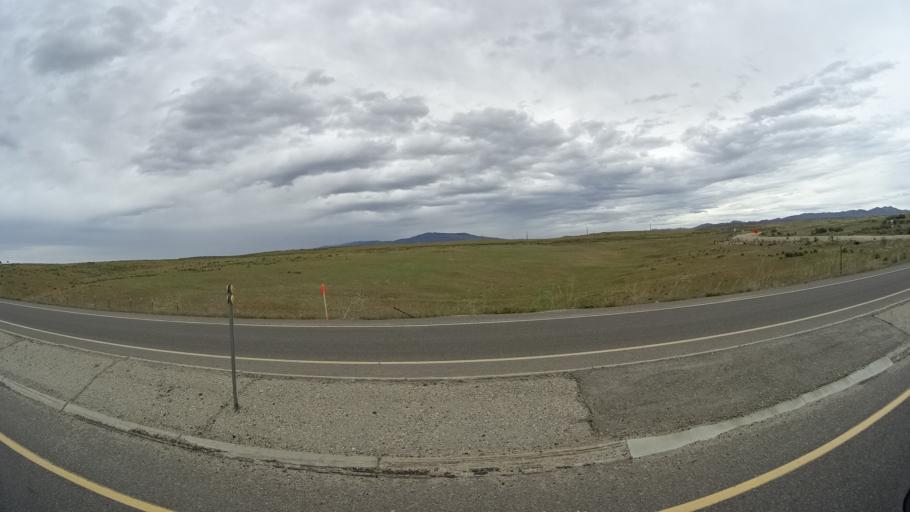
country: US
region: Idaho
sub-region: Ada County
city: Boise
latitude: 43.4665
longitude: -116.0924
